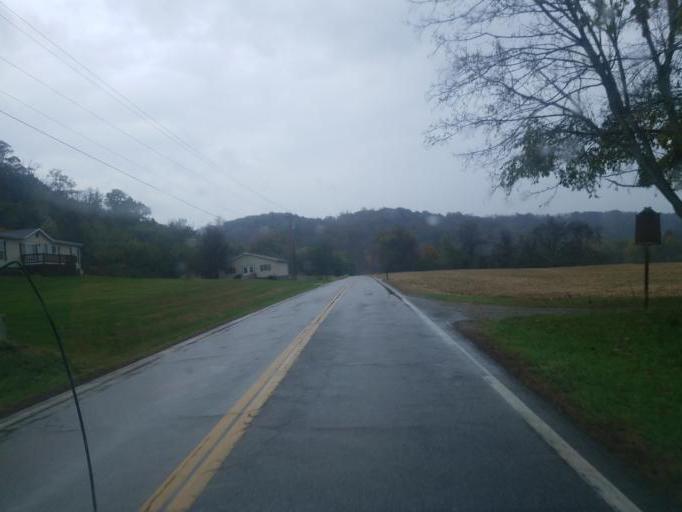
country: US
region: Ohio
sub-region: Morgan County
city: McConnelsville
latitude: 39.5699
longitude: -81.7785
